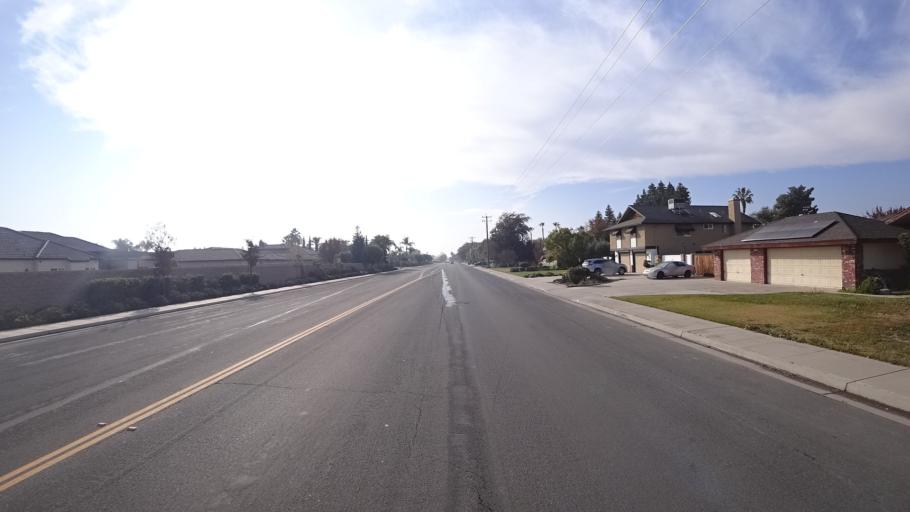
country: US
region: California
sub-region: Kern County
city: Rosedale
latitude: 35.3720
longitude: -119.1545
